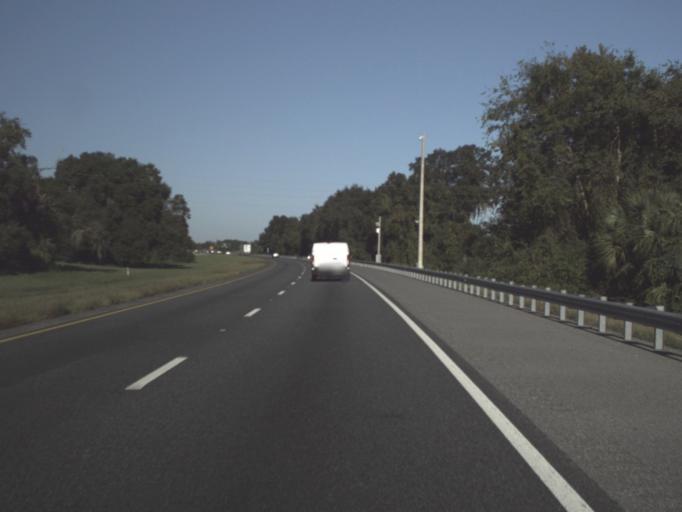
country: US
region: Florida
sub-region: Sumter County
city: Wildwood
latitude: 28.7874
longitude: -81.9810
